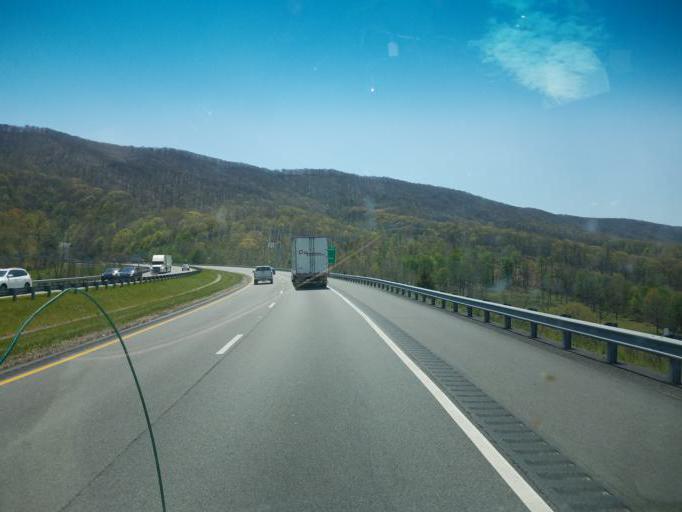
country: US
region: Virginia
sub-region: Bland County
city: Bland
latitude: 37.0468
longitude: -81.1394
